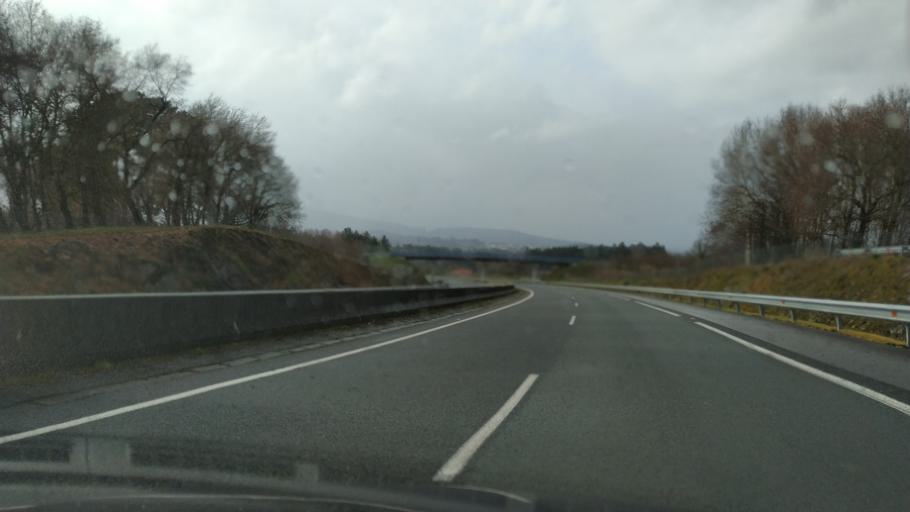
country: ES
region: Galicia
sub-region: Provincia de Pontevedra
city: Silleda
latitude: 42.7180
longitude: -8.2606
